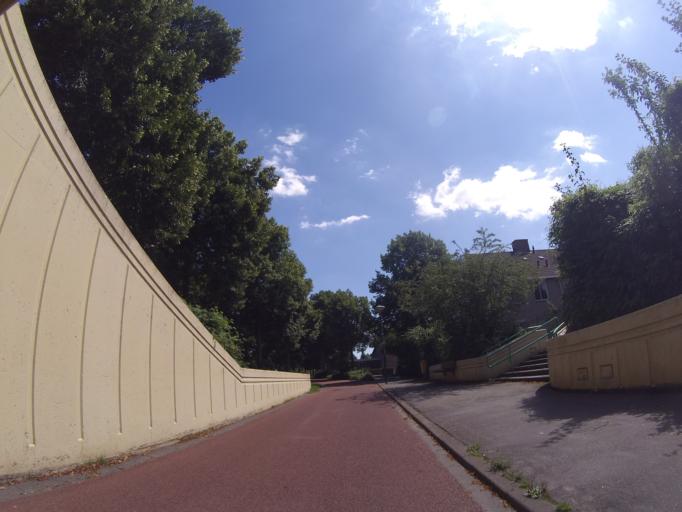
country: NL
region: Utrecht
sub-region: Stichtse Vecht
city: Spechtenkamp
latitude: 52.1412
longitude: 5.0136
